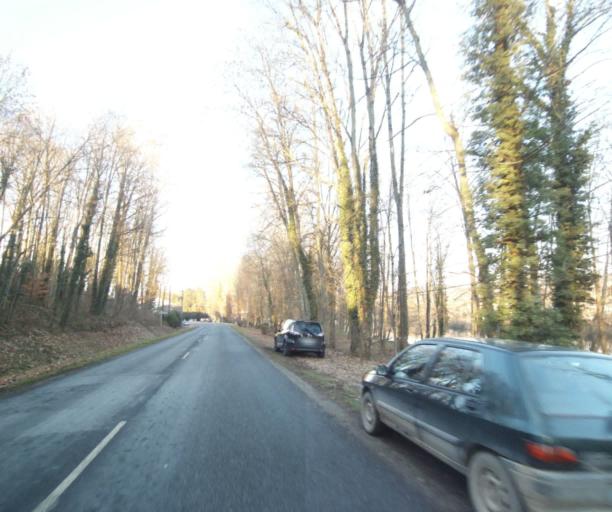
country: FR
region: Champagne-Ardenne
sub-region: Departement de la Haute-Marne
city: Bienville
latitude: 48.5800
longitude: 5.0396
